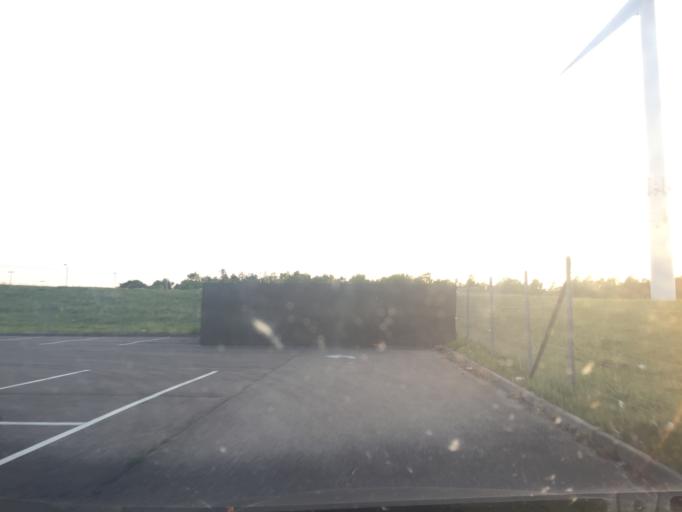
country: DK
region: Capital Region
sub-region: Hoje-Taastrup Kommune
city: Taastrup
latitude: 55.6614
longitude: 12.2851
